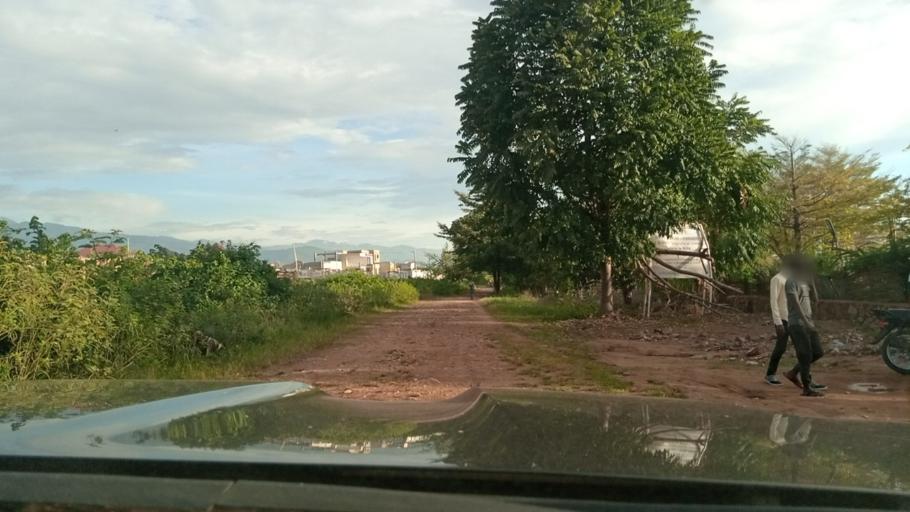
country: BI
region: Bujumbura Mairie
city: Bujumbura
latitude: -3.4454
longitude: 29.3454
